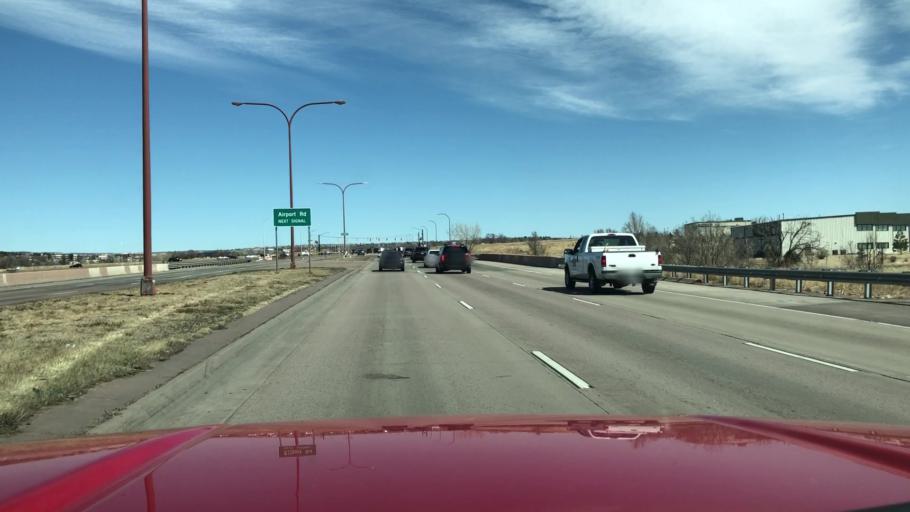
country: US
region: Colorado
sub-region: El Paso County
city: Cimarron Hills
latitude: 38.8216
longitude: -104.7266
